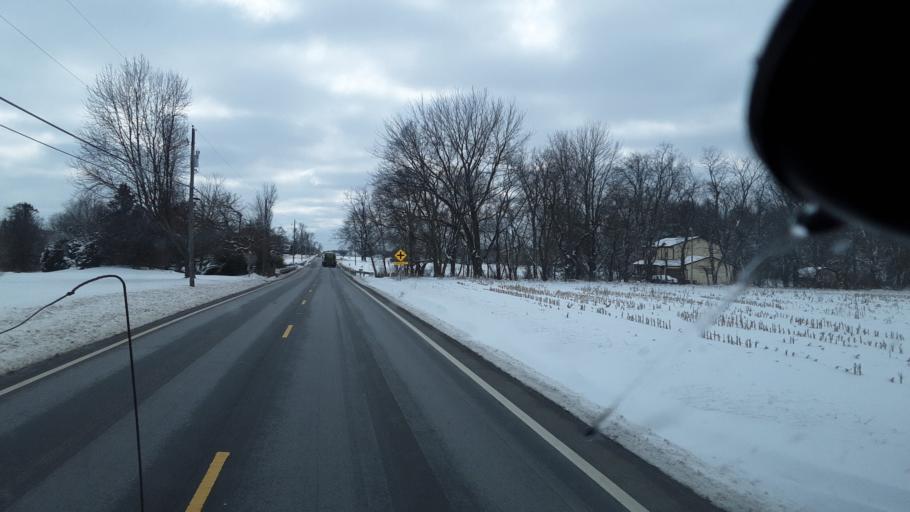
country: US
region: Ohio
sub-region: Delaware County
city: Sunbury
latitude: 40.2059
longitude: -82.8044
